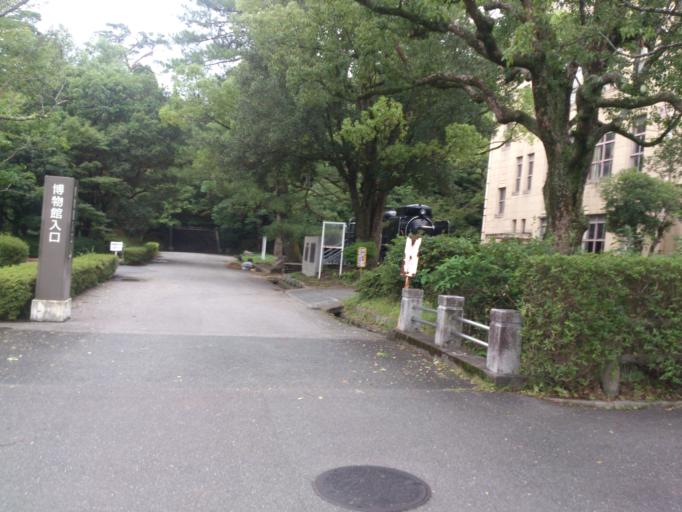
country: JP
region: Yamaguchi
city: Yamaguchi-shi
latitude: 34.1835
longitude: 131.4730
